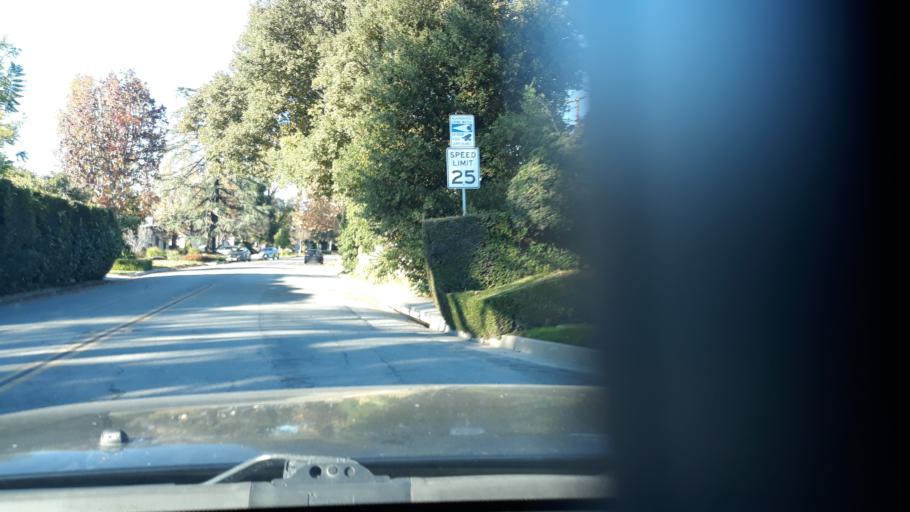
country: US
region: California
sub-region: Los Angeles County
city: San Marino
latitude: 34.1192
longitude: -118.0976
